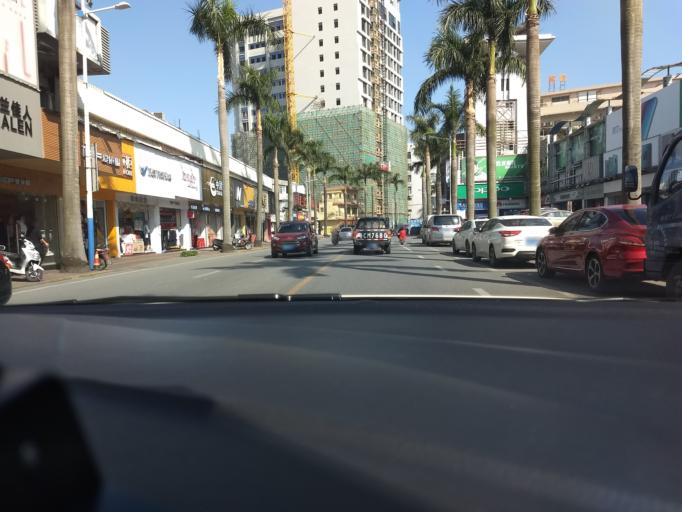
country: CN
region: Guangdong
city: Dagang
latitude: 22.8065
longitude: 113.4029
